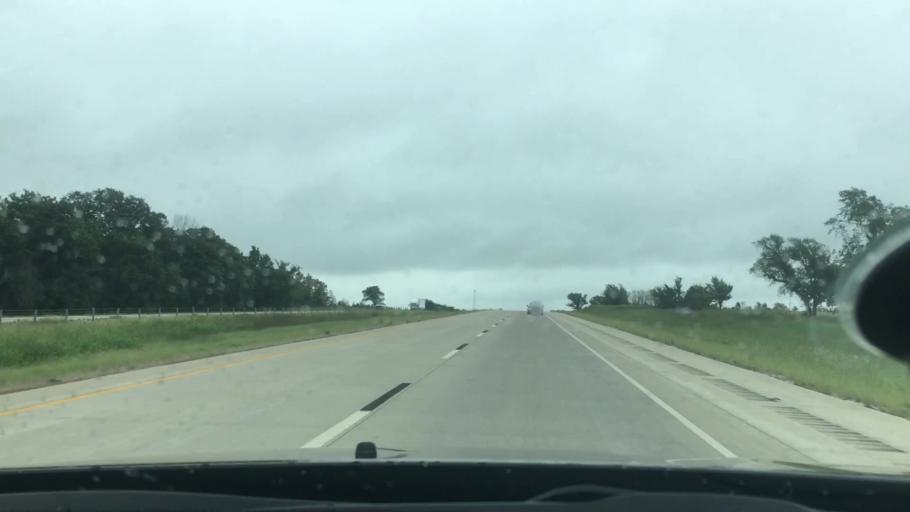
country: US
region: Oklahoma
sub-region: Okmulgee County
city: Wilson
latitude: 35.4274
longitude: -96.0768
